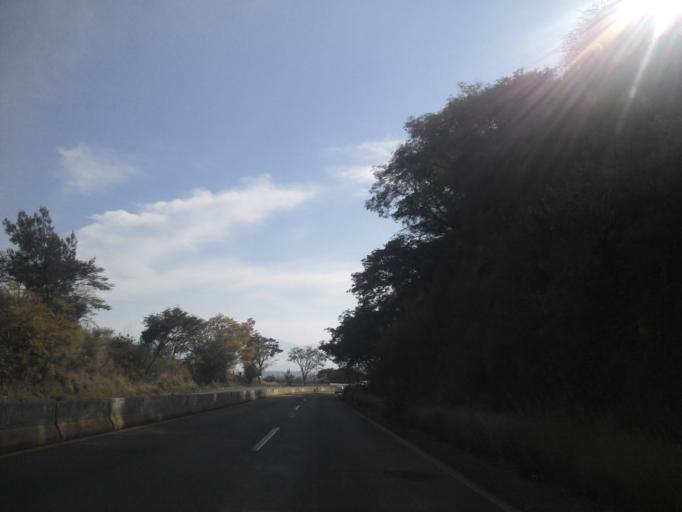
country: MX
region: Jalisco
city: Ixtlahuacan de los Membrillos
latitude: 20.3296
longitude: -103.1837
